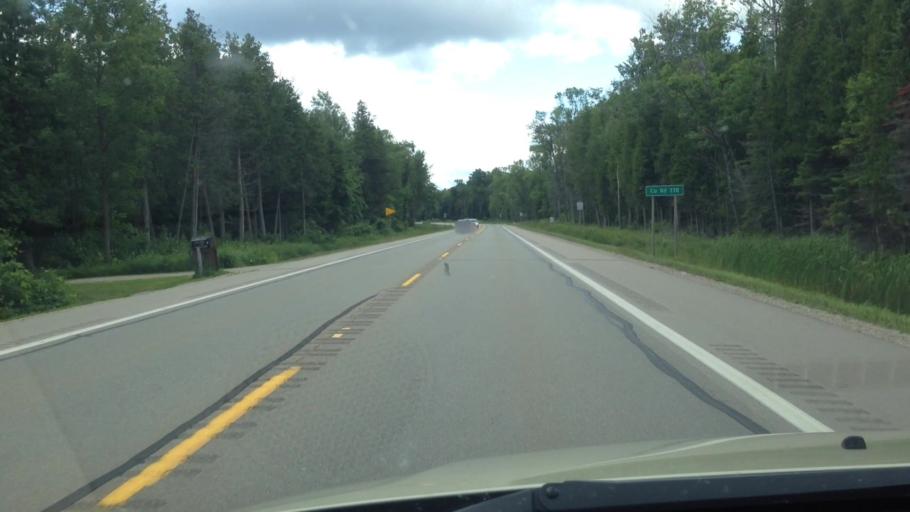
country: US
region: Michigan
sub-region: Menominee County
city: Menominee
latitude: 45.3115
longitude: -87.4367
